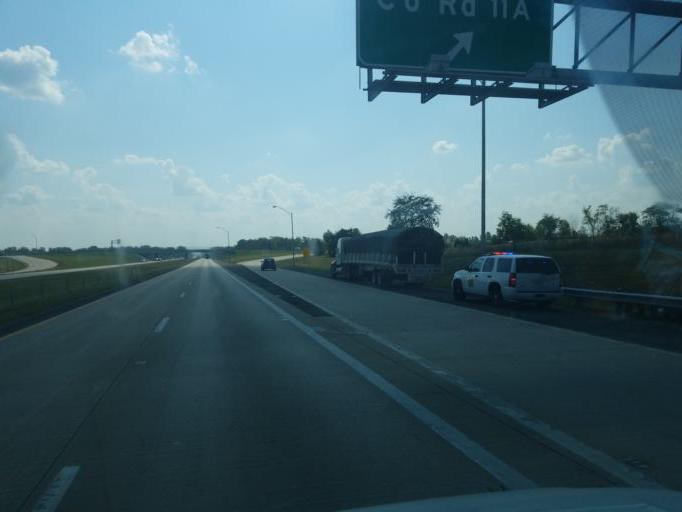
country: US
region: Indiana
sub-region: DeKalb County
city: Auburn
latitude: 41.3312
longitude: -85.0880
